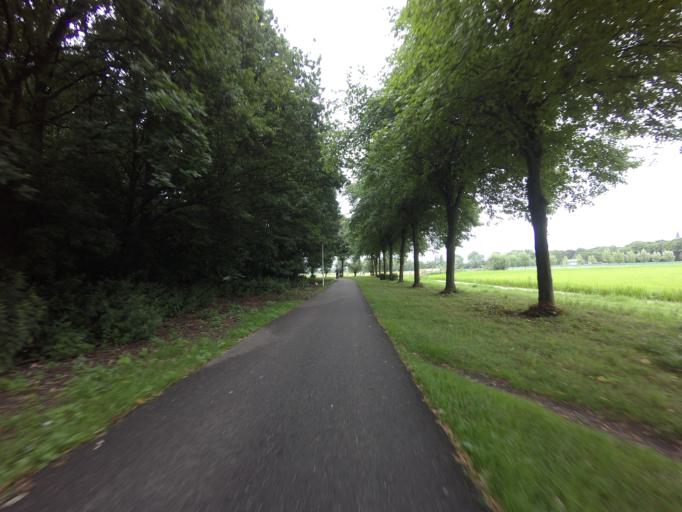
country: NL
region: South Holland
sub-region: Gemeente Teylingen
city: Voorhout
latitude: 52.2007
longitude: 4.4937
